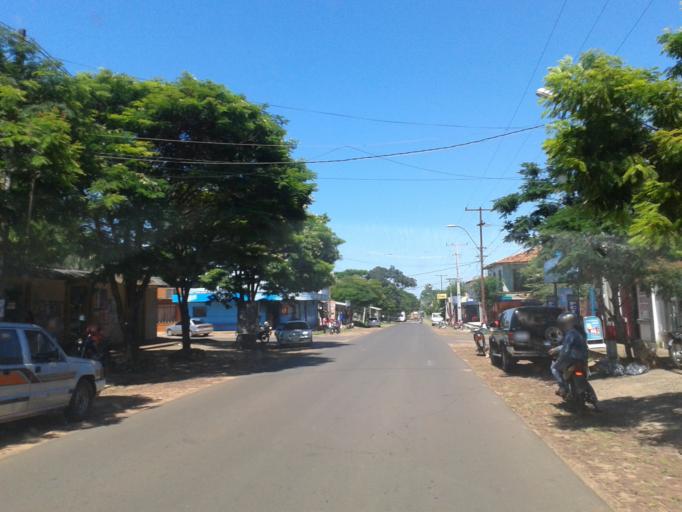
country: PY
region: Misiones
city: Santa Rosa
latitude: -26.8874
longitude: -56.8522
